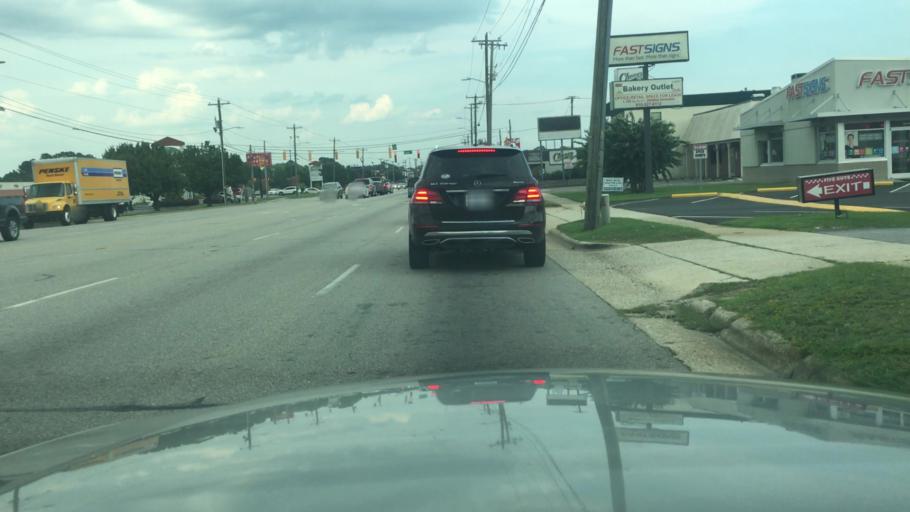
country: US
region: North Carolina
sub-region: Cumberland County
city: Fayetteville
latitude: 35.0453
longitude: -78.9258
